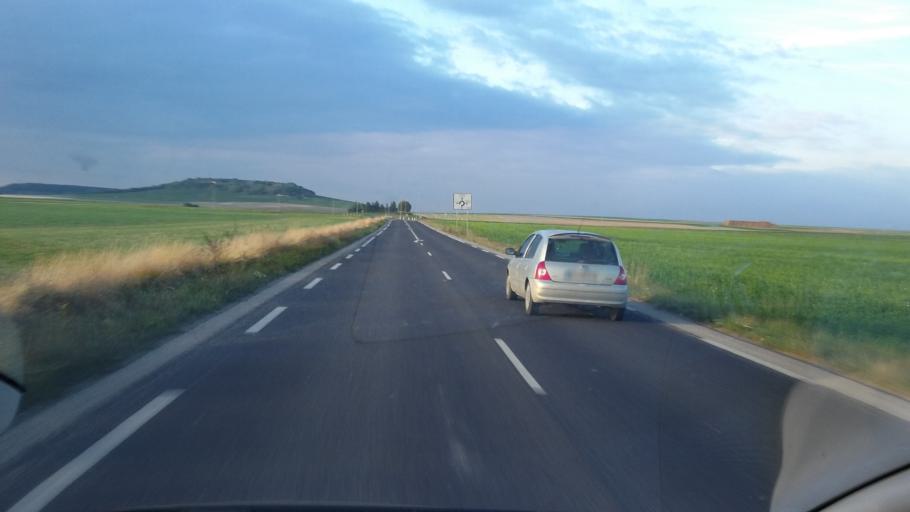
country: FR
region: Champagne-Ardenne
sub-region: Departement de la Marne
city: Vertus
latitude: 48.8351
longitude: 3.9984
